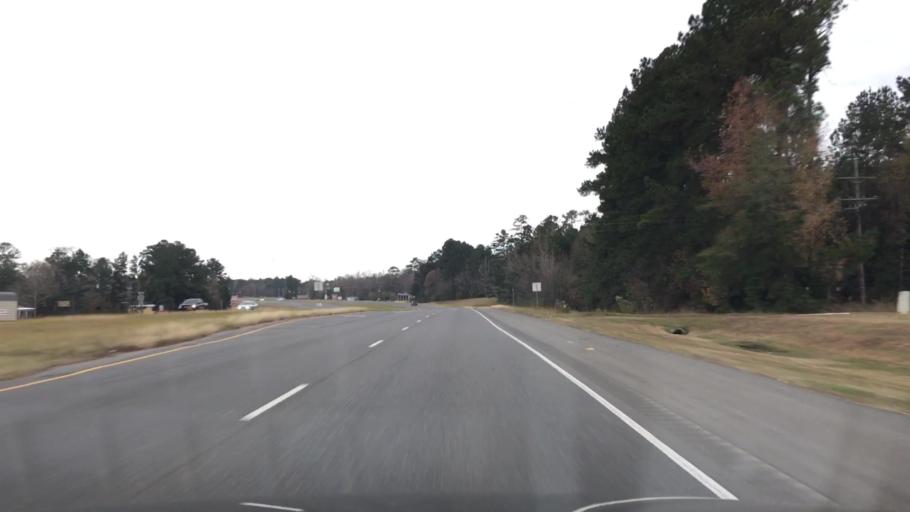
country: US
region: Louisiana
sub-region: Vernon Parish
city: New Llano
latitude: 31.0722
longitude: -93.2740
